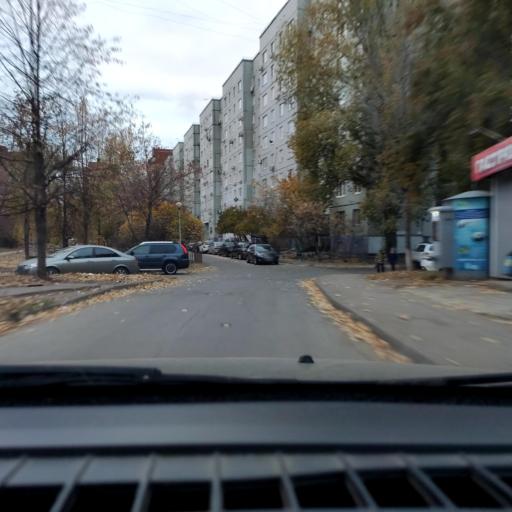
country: RU
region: Samara
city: Tol'yatti
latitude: 53.5440
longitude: 49.3401
